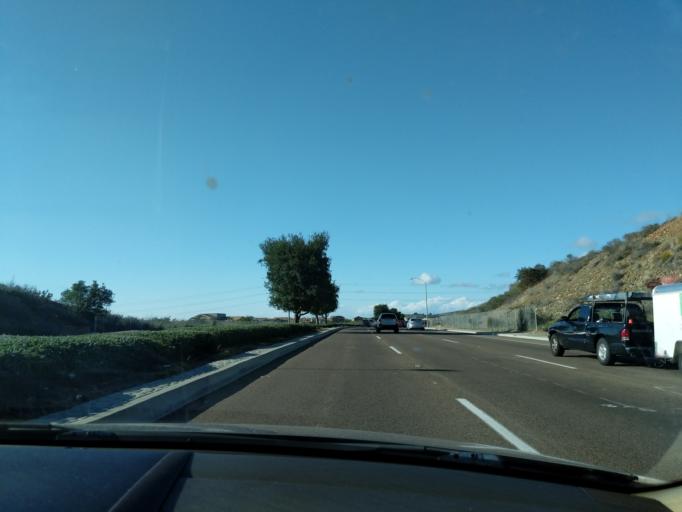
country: US
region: California
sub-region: San Diego County
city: Lake San Marcos
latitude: 33.0916
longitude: -117.2251
